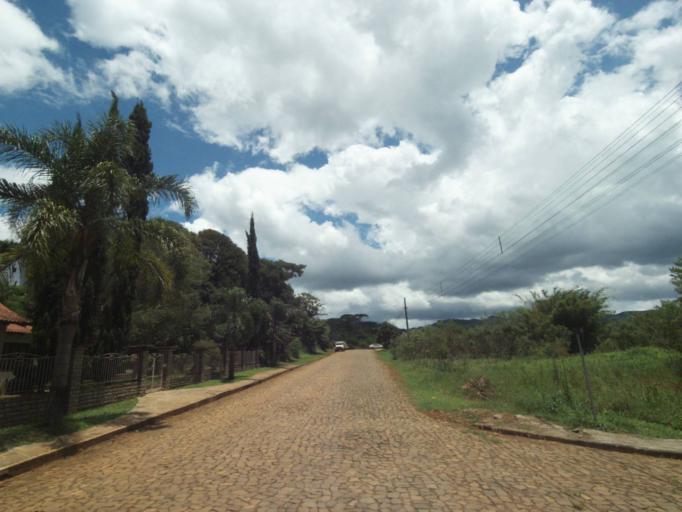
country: BR
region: Parana
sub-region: Uniao Da Vitoria
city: Uniao da Vitoria
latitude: -26.1596
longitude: -51.5519
